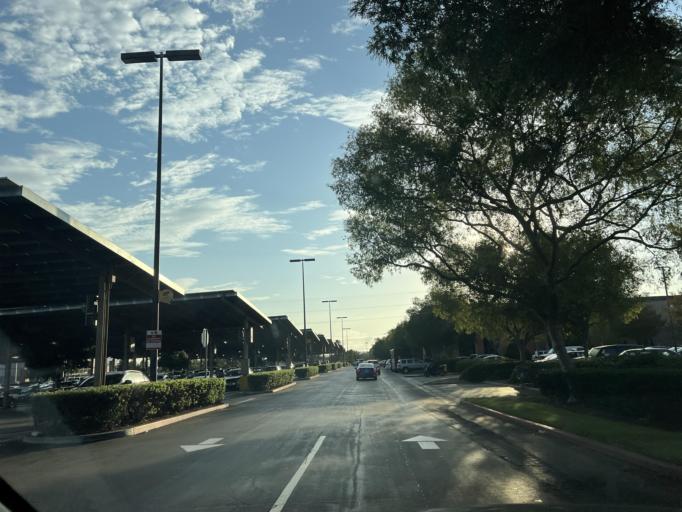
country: US
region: California
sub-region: San Diego County
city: La Jolla
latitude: 32.8307
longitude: -117.1642
